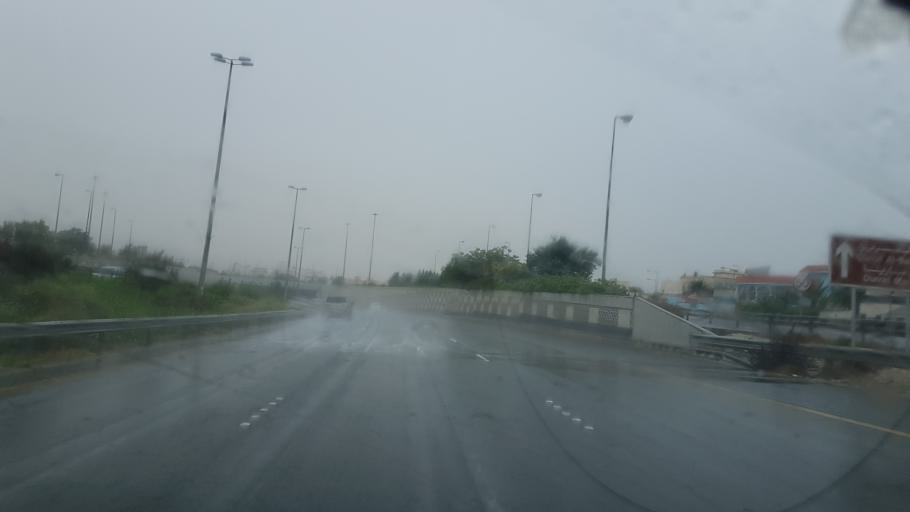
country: BH
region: Central Governorate
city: Madinat Hamad
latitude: 26.1244
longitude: 50.5062
